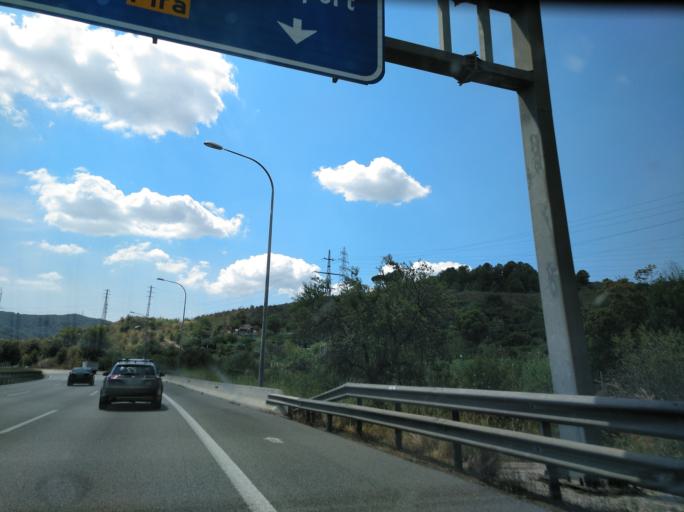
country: ES
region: Catalonia
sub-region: Provincia de Barcelona
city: Montcada i Reixac
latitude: 41.4710
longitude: 2.1784
